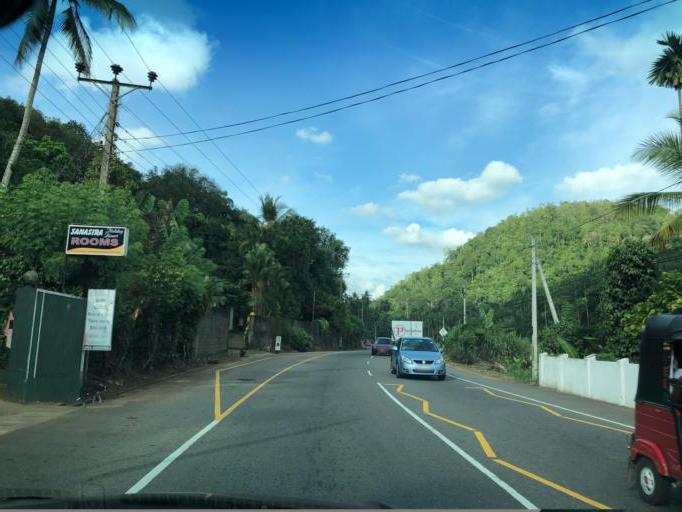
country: LK
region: Western
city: Horawala Junction
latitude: 6.5216
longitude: 80.0832
